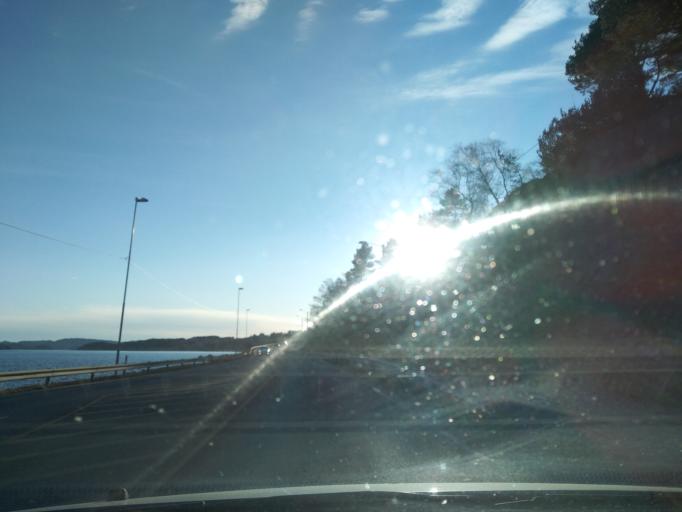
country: NO
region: Rogaland
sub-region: Tysvaer
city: Aksdal
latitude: 59.4999
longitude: 5.5766
